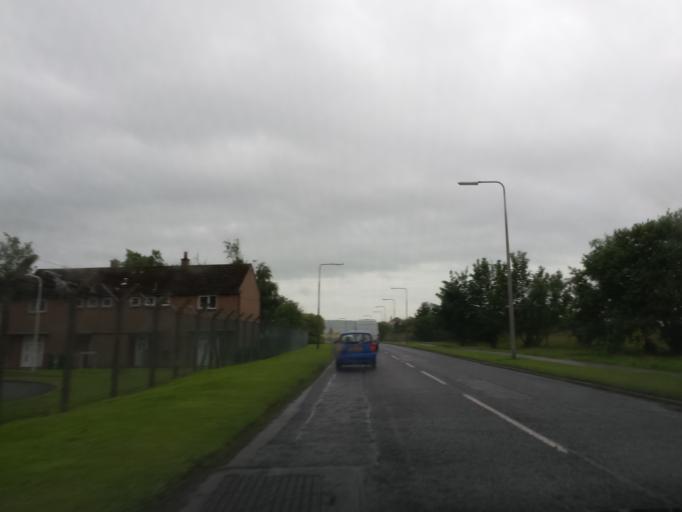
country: GB
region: Scotland
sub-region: Fife
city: Leuchars
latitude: 56.3789
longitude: -2.8898
